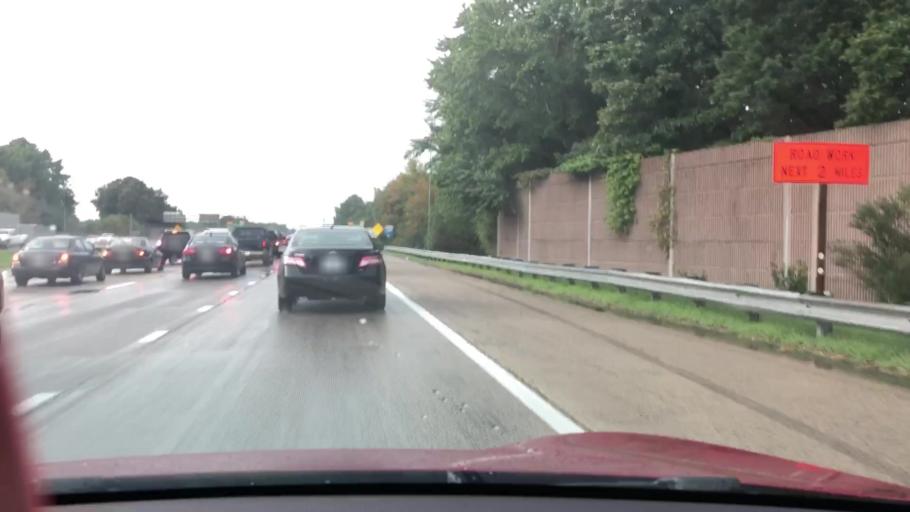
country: US
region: Virginia
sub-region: City of Chesapeake
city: Chesapeake
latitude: 36.8235
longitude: -76.1948
